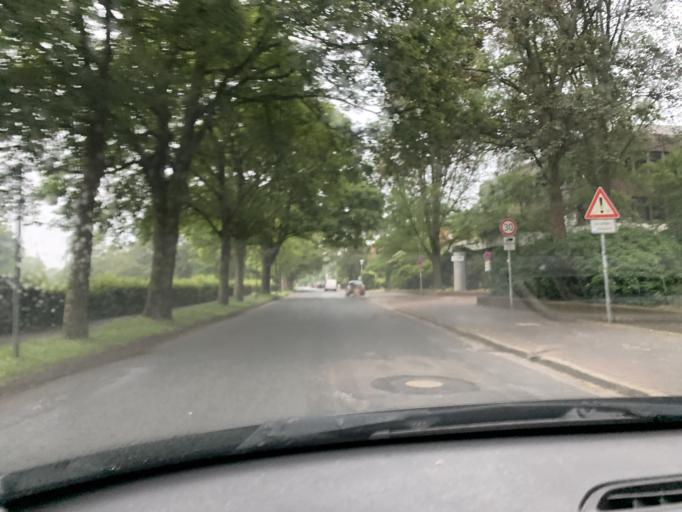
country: DE
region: Lower Saxony
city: Oldenburg
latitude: 53.1397
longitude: 8.1963
